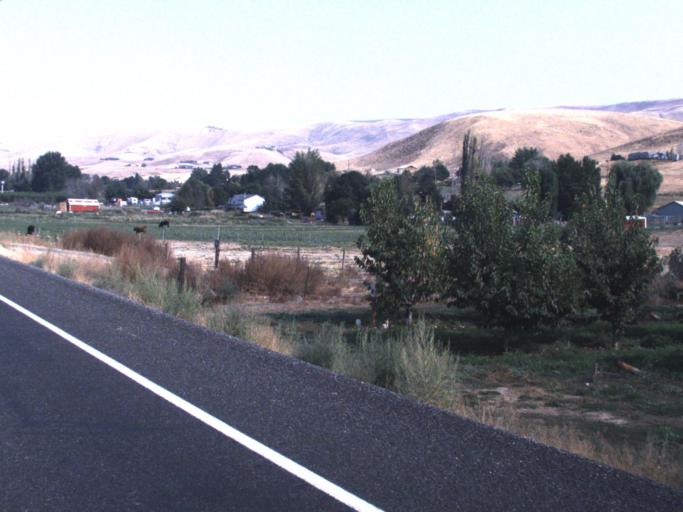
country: US
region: Washington
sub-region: Yakima County
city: Grandview
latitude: 46.1858
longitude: -119.8547
